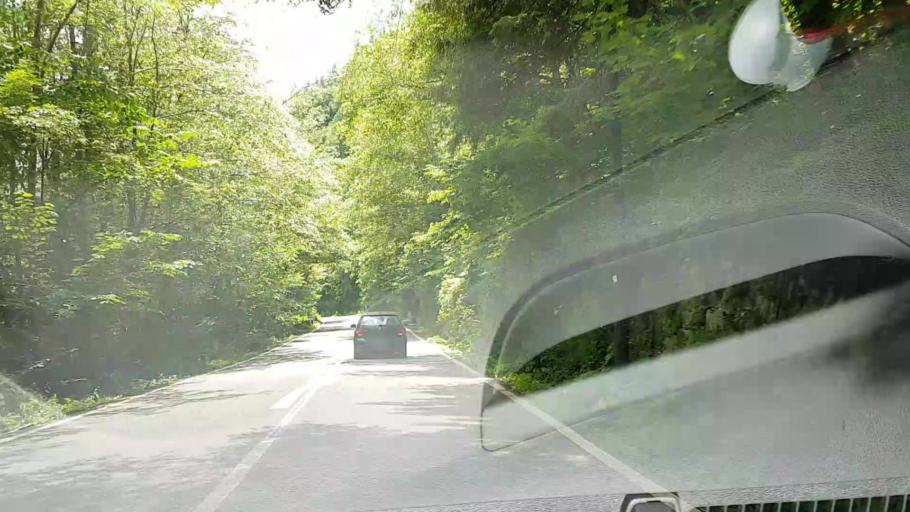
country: RO
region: Suceava
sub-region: Comuna Crucea
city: Crucea
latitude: 47.2940
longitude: 25.6317
